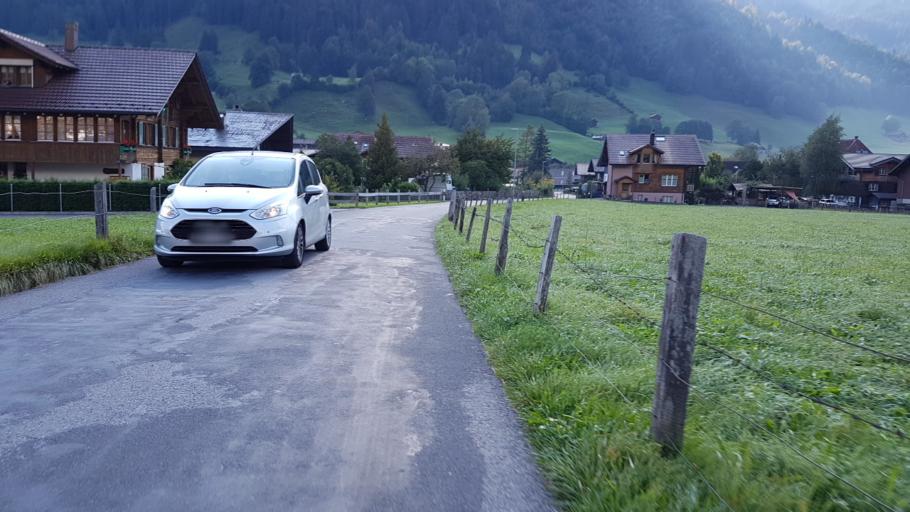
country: CH
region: Bern
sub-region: Frutigen-Niedersimmental District
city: Frutigen
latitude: 46.5844
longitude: 7.6545
